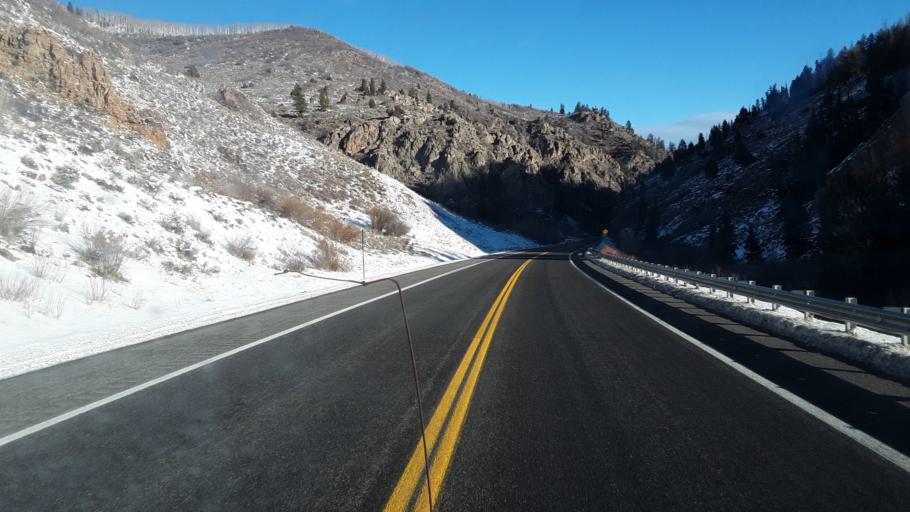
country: US
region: Colorado
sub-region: Hinsdale County
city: Lake City
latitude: 38.3966
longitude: -107.4138
